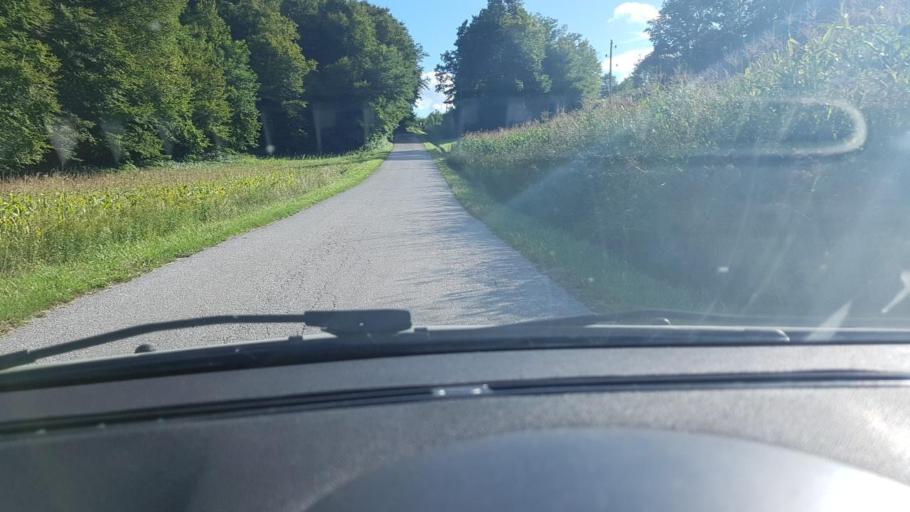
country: HR
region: Krapinsko-Zagorska
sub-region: Grad Krapina
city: Krapina
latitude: 46.1506
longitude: 15.8418
